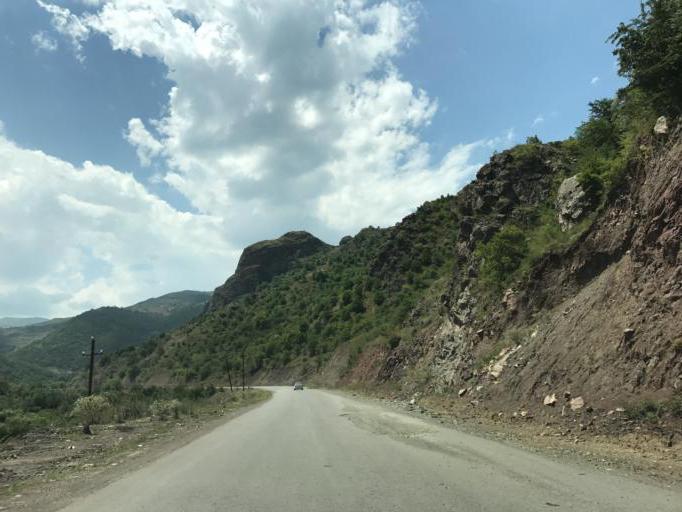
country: AZ
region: Kalbacar Rayonu
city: Kerbakhiar
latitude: 40.2326
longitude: 46.1025
